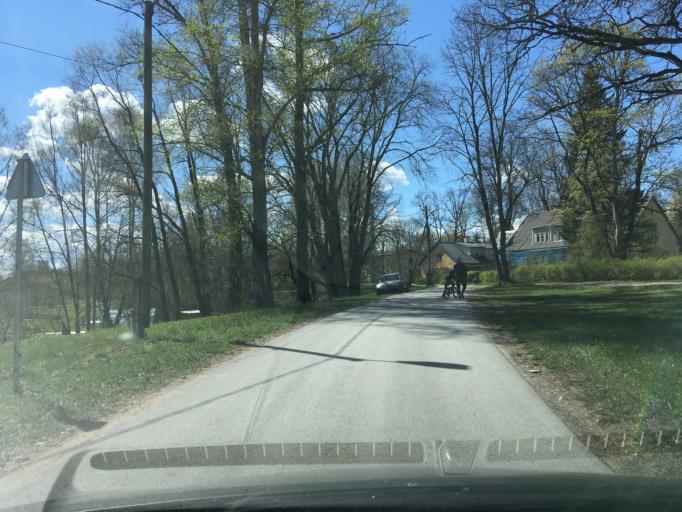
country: EE
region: Harju
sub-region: Raasiku vald
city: Arukula
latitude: 59.2062
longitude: 25.1075
